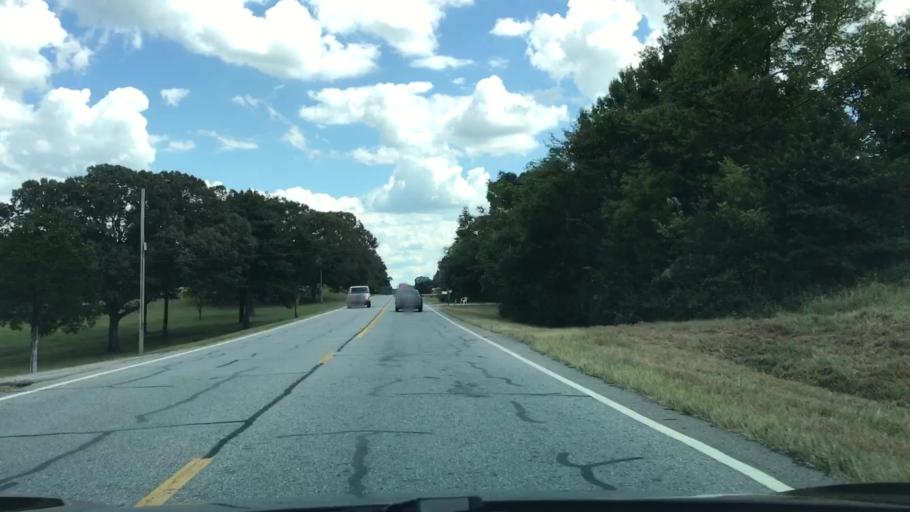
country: US
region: Georgia
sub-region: Oconee County
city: Watkinsville
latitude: 33.8011
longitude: -83.3383
